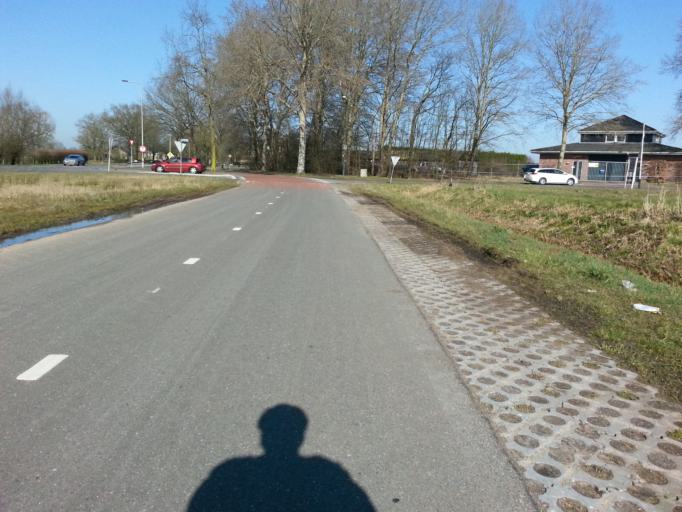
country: NL
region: Utrecht
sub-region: Gemeente Utrechtse Heuvelrug
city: Maarsbergen
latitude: 52.0668
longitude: 5.4100
